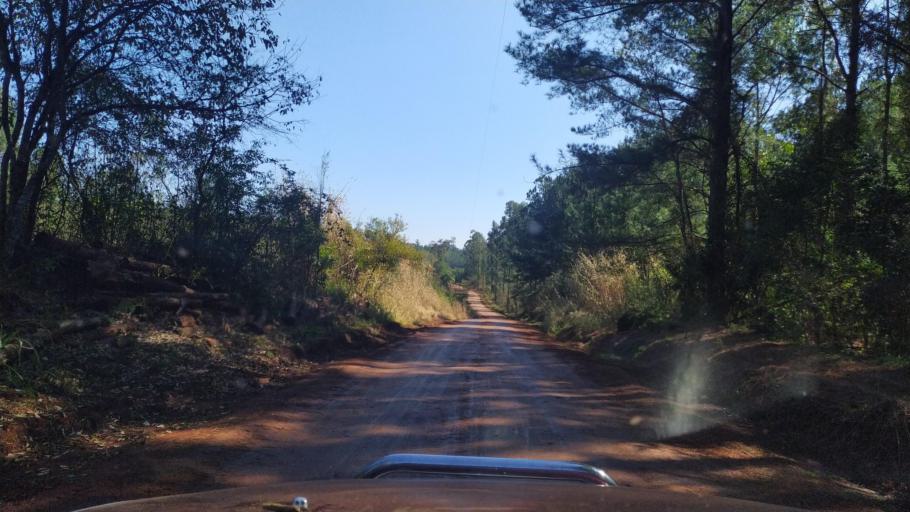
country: AR
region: Misiones
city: El Alcazar
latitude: -26.7335
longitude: -54.6702
